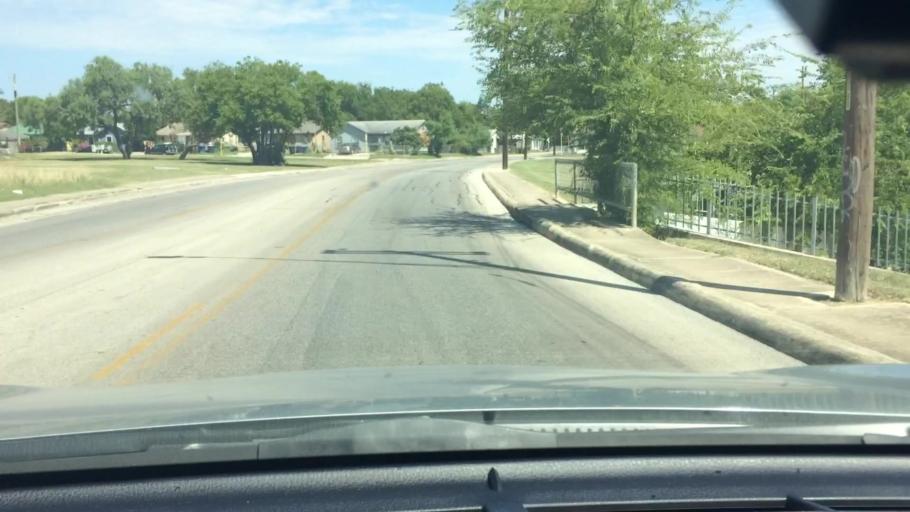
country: US
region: Texas
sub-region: Bexar County
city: San Antonio
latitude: 29.3896
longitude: -98.4329
